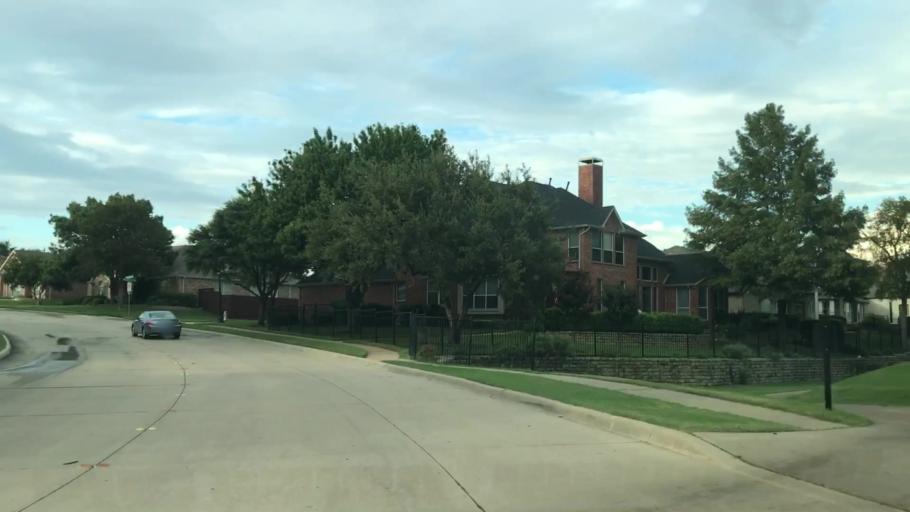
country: US
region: Texas
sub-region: Denton County
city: The Colony
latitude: 33.0442
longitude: -96.8485
